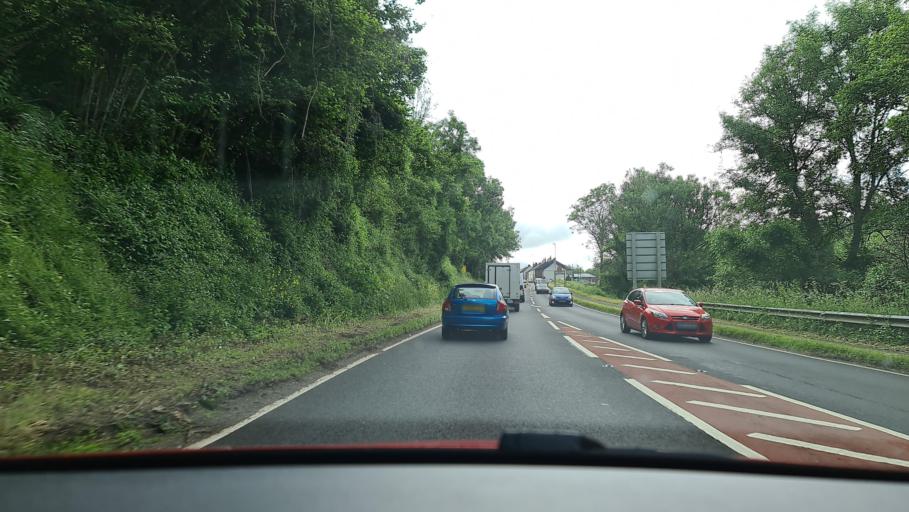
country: GB
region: England
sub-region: Cornwall
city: Pillaton
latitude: 50.4135
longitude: -4.3311
